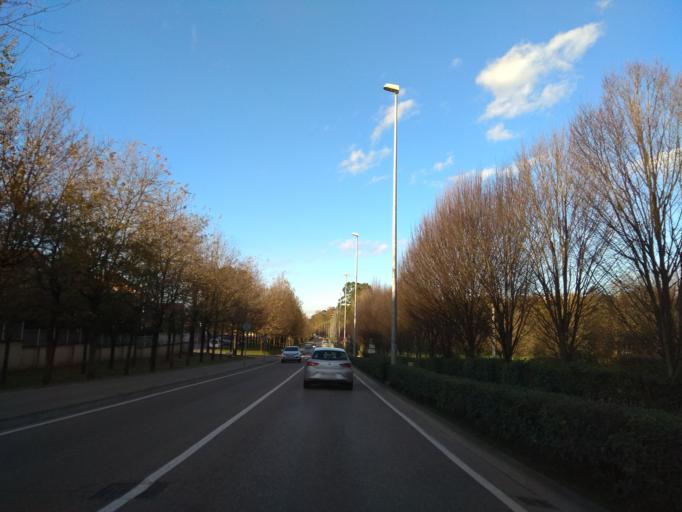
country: ES
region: Cantabria
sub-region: Provincia de Cantabria
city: Torrelavega
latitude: 43.3468
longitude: -4.0393
